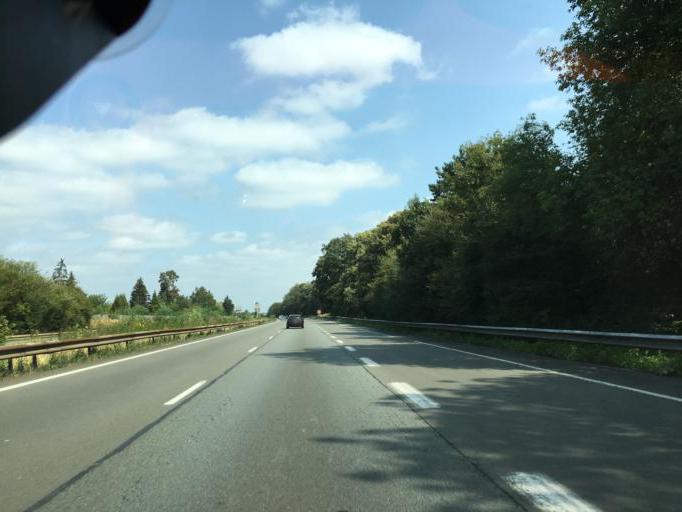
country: FR
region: Nord-Pas-de-Calais
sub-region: Departement du Nord
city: Wavrechain-sous-Denain
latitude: 50.3160
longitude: 3.4113
